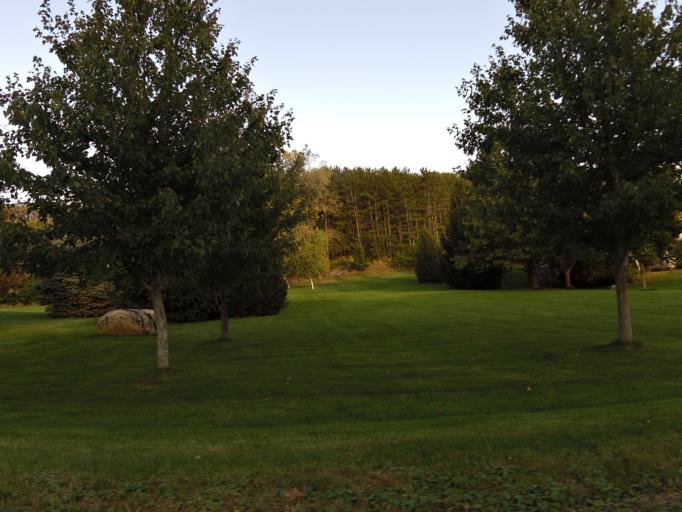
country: US
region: Minnesota
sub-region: Washington County
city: Bayport
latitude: 44.9819
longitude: -92.8056
